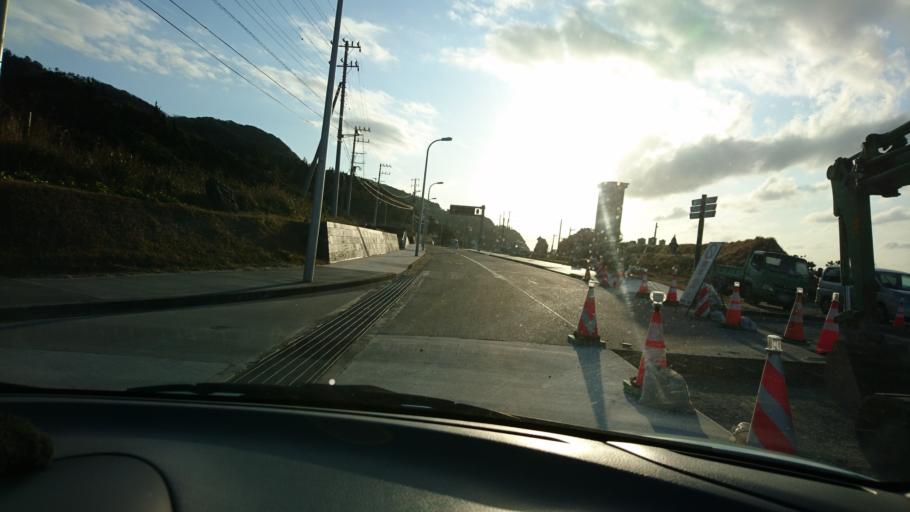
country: JP
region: Shizuoka
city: Shimoda
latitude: 34.3709
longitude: 139.2497
